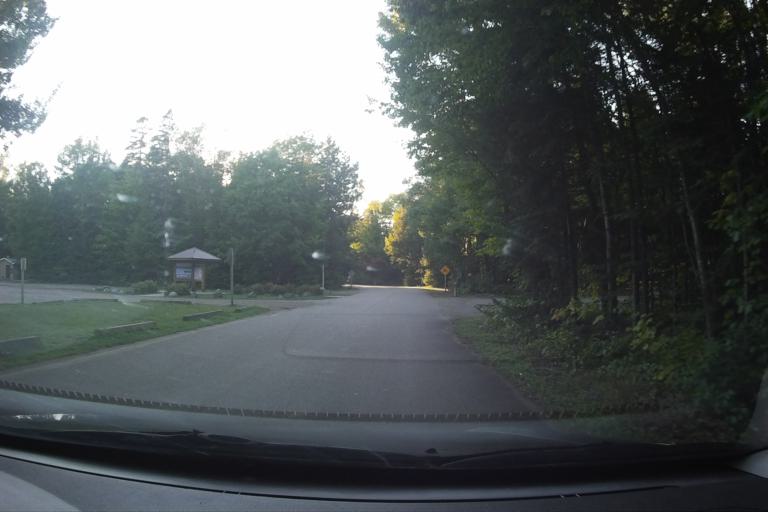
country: CA
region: Ontario
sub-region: Algoma
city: Sault Ste. Marie
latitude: 46.9697
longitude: -84.6886
